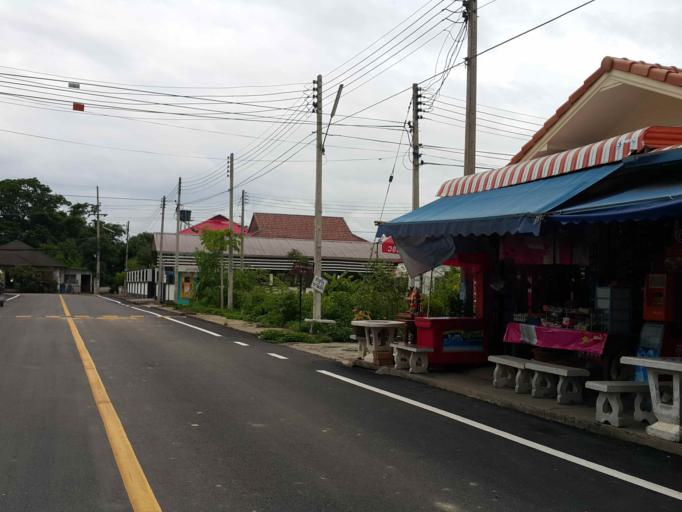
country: TH
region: Chiang Mai
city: San Sai
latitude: 18.8249
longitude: 99.0559
